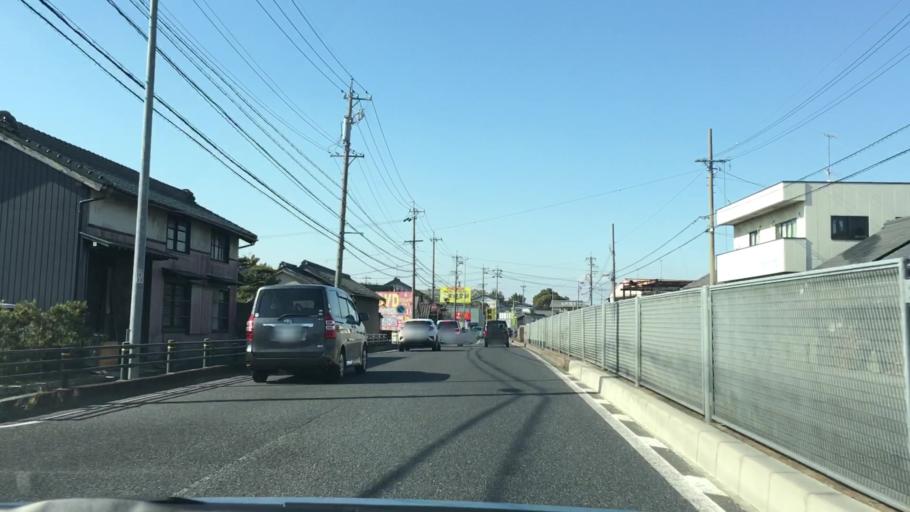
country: JP
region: Aichi
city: Anjo
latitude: 34.9718
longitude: 137.1227
